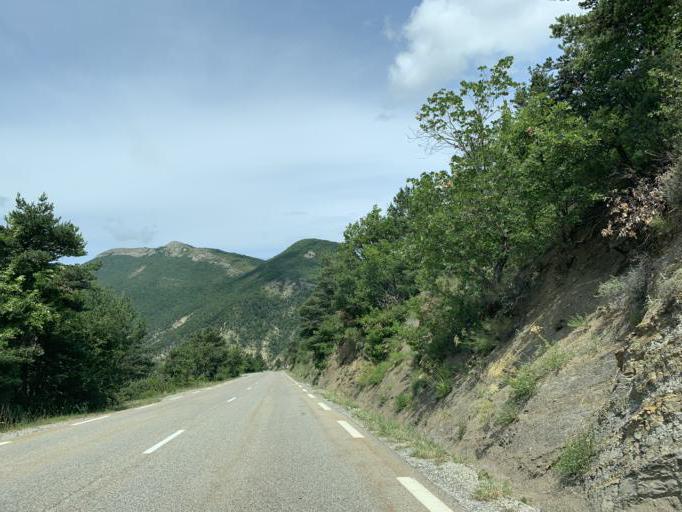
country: FR
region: Provence-Alpes-Cote d'Azur
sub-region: Departement des Hautes-Alpes
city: Veynes
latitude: 44.5371
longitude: 5.7884
